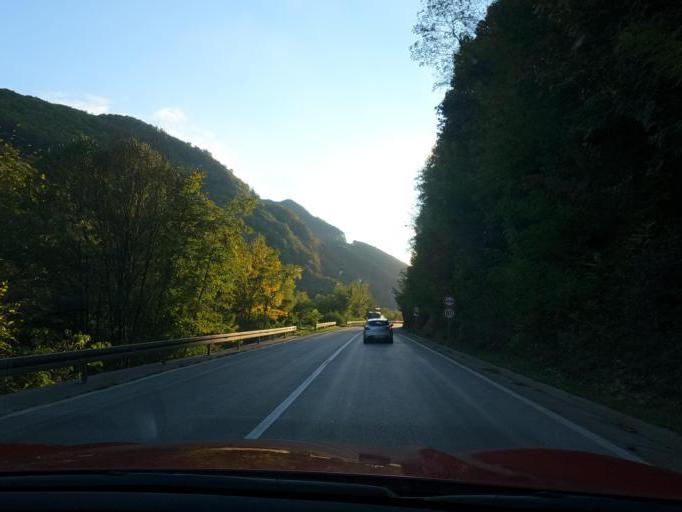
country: RS
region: Central Serbia
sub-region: Moravicki Okrug
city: Lucani
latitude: 43.9001
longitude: 20.1757
